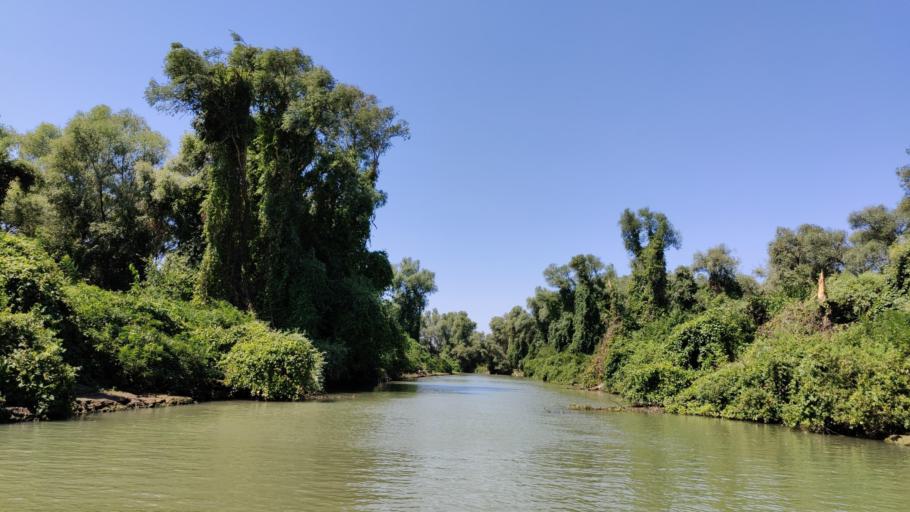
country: RO
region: Tulcea
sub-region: Comuna Pardina
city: Pardina
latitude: 45.2551
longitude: 28.9433
